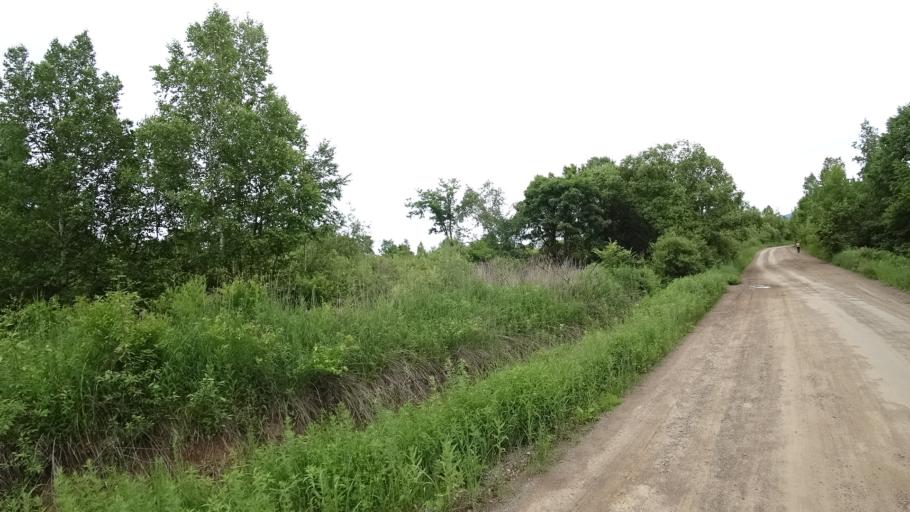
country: RU
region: Primorskiy
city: Arsen'yev
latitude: 44.1937
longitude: 133.3099
